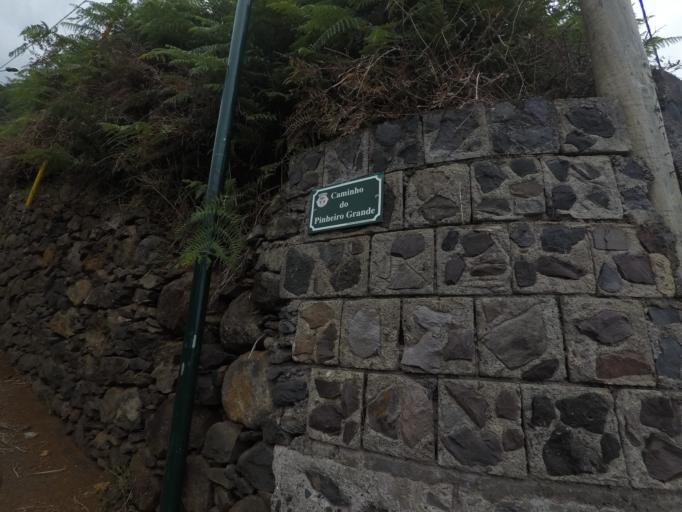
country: PT
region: Madeira
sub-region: Santana
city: Santana
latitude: 32.7879
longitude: -16.8586
